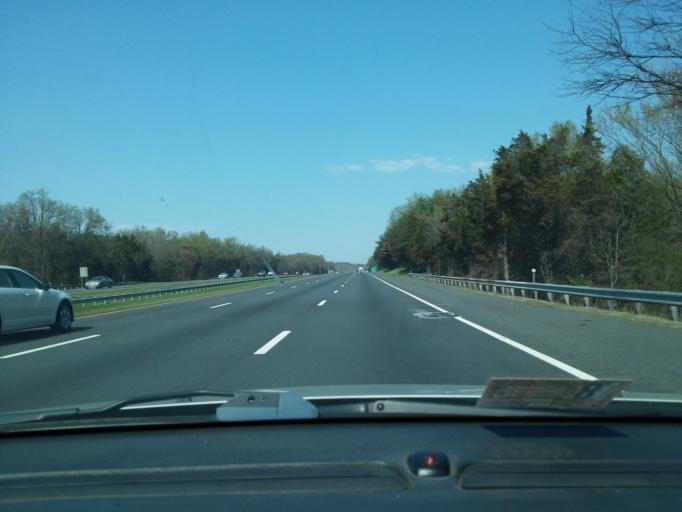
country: US
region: New Jersey
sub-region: Somerset County
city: Bedminster
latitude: 40.6438
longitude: -74.7016
